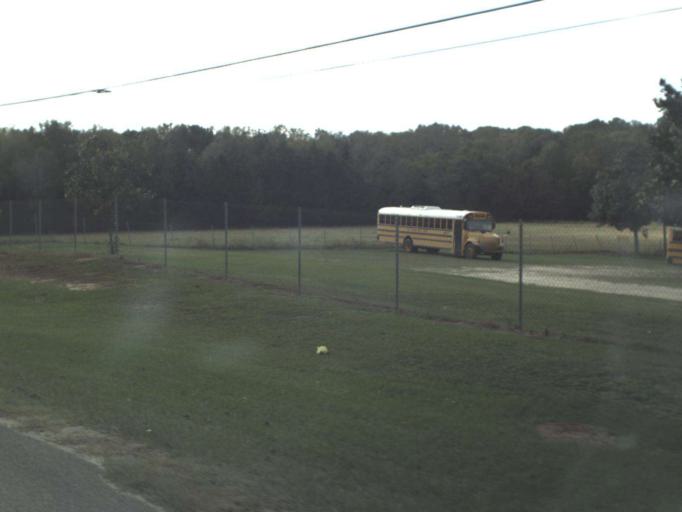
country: US
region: Florida
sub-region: Jackson County
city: Marianna
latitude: 30.7681
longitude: -85.2546
